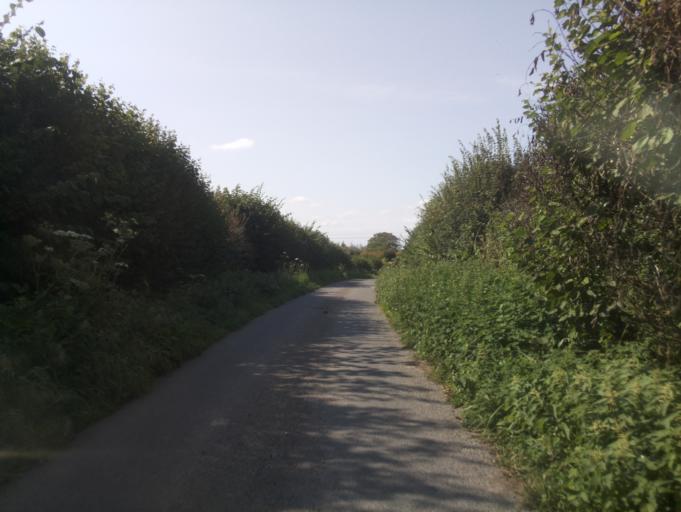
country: GB
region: England
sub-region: Gloucestershire
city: Dursley
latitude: 51.7072
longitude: -2.3169
